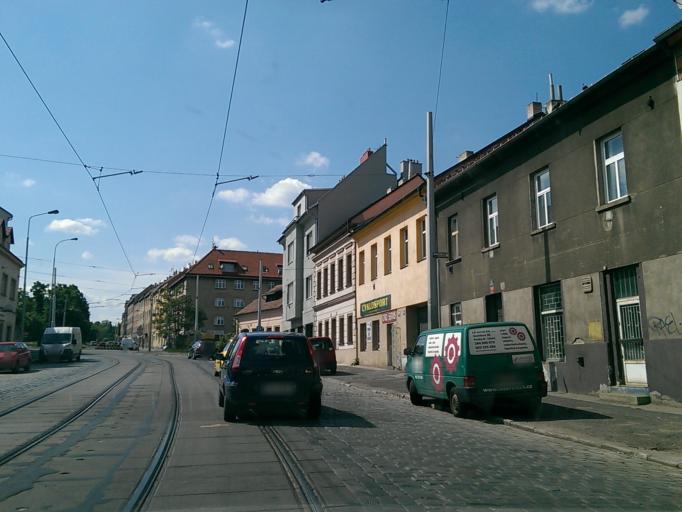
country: CZ
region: Praha
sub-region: Praha 8
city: Liben
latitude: 50.1142
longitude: 14.4755
